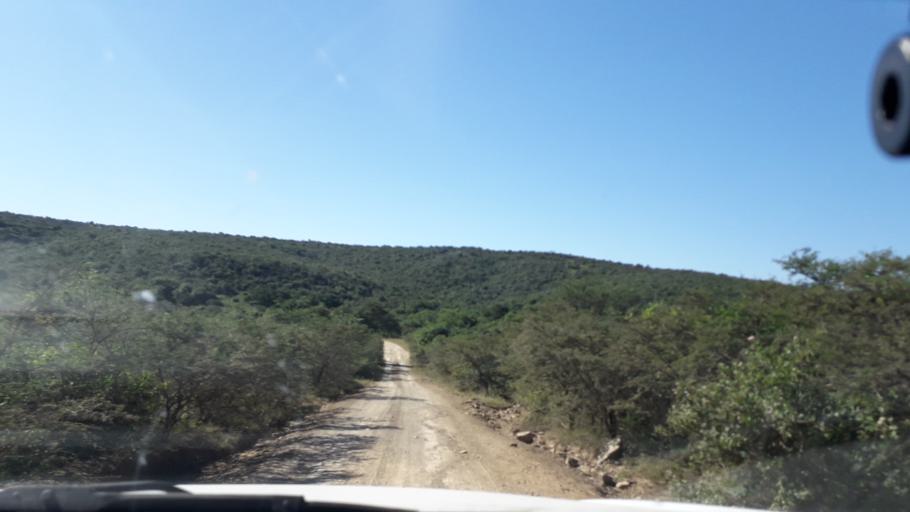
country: ZA
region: Eastern Cape
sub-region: Amathole District Municipality
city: Komga
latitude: -32.7693
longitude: 27.9614
